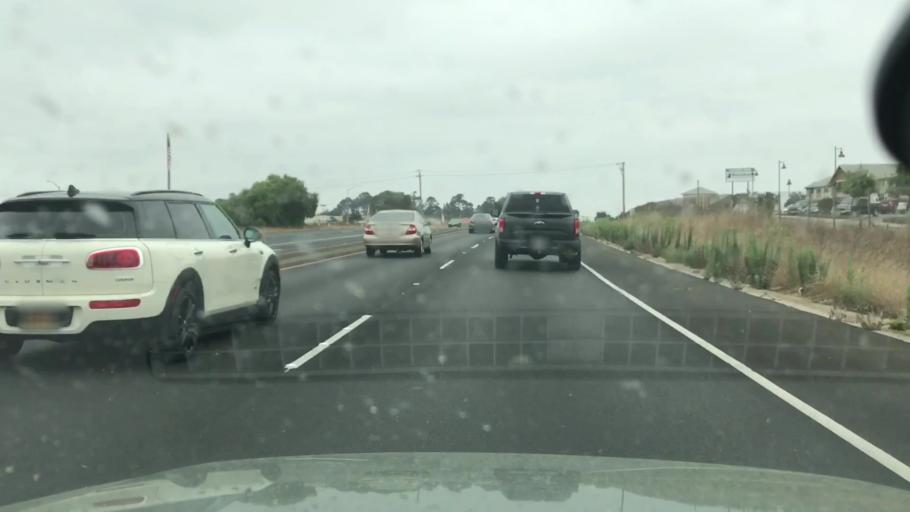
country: US
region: California
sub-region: Santa Barbara County
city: Orcutt
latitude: 34.8955
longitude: -120.4363
